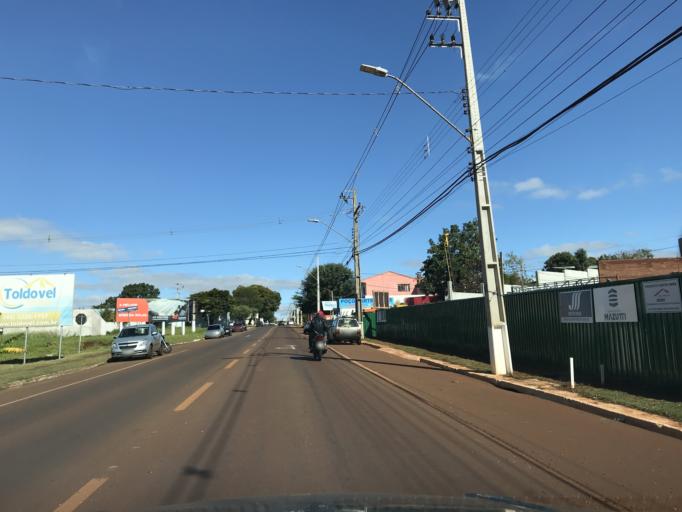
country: BR
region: Parana
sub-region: Cascavel
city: Cascavel
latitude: -24.9292
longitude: -53.4749
